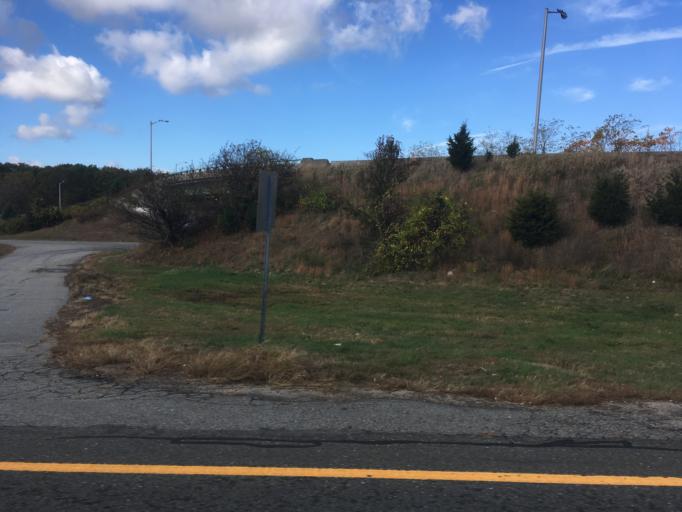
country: US
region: Rhode Island
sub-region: Providence County
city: Cranston
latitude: 41.7525
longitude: -71.4814
